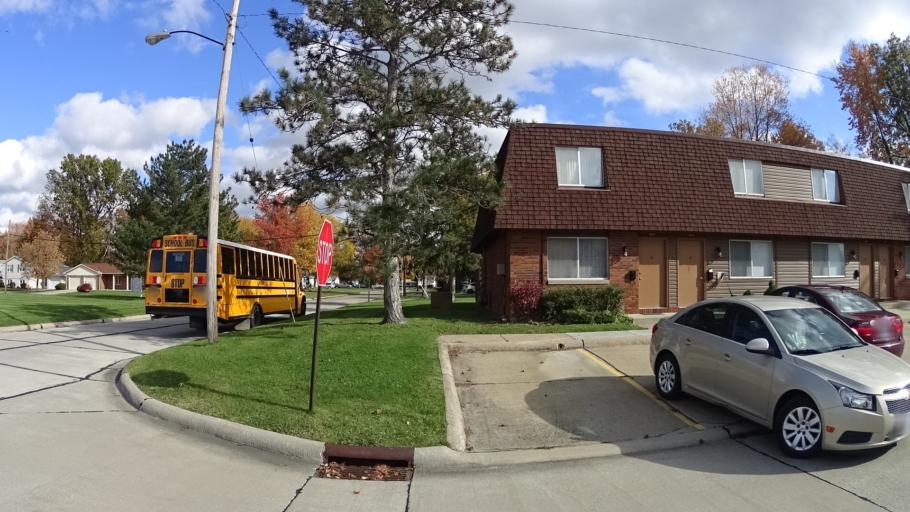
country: US
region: Ohio
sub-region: Lorain County
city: Lorain
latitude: 41.4293
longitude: -82.1974
